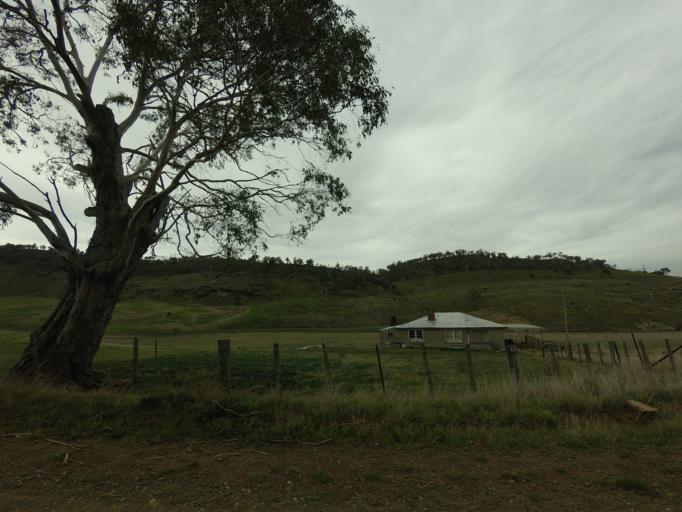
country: AU
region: Tasmania
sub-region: Derwent Valley
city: New Norfolk
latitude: -42.4039
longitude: 146.9203
